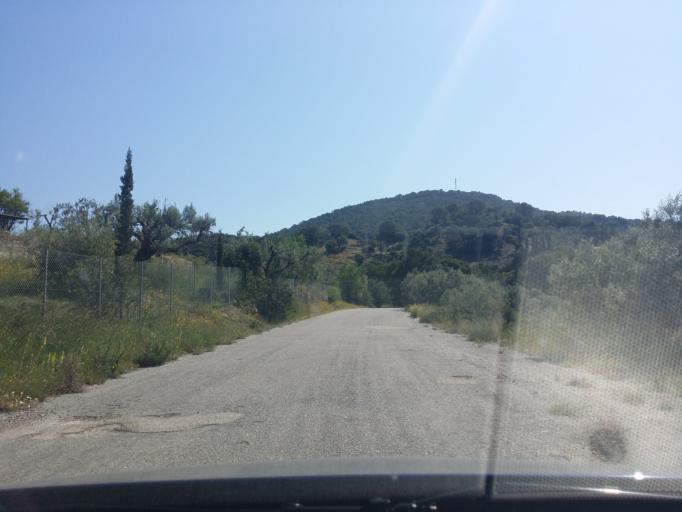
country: GR
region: Attica
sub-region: Nomos Piraios
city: Poros
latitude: 37.5224
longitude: 23.4824
